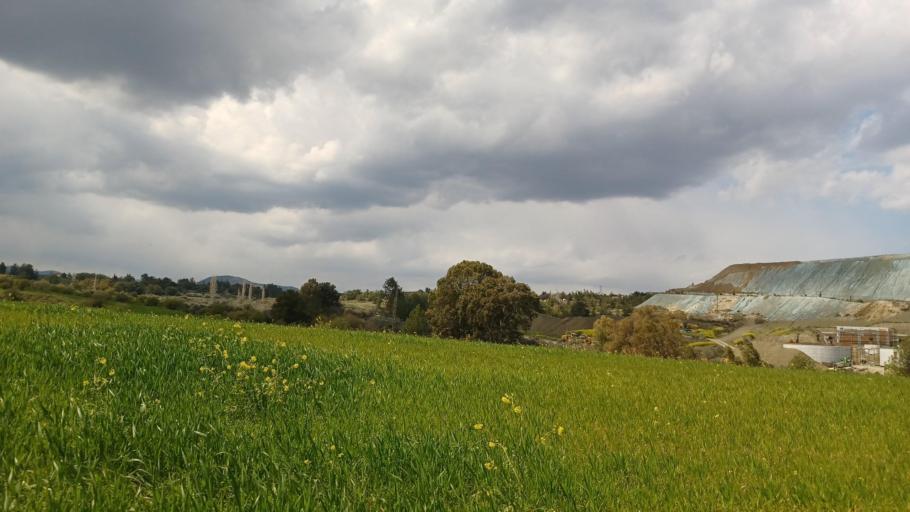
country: CY
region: Lefkosia
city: Lefka
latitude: 35.0843
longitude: 32.9038
